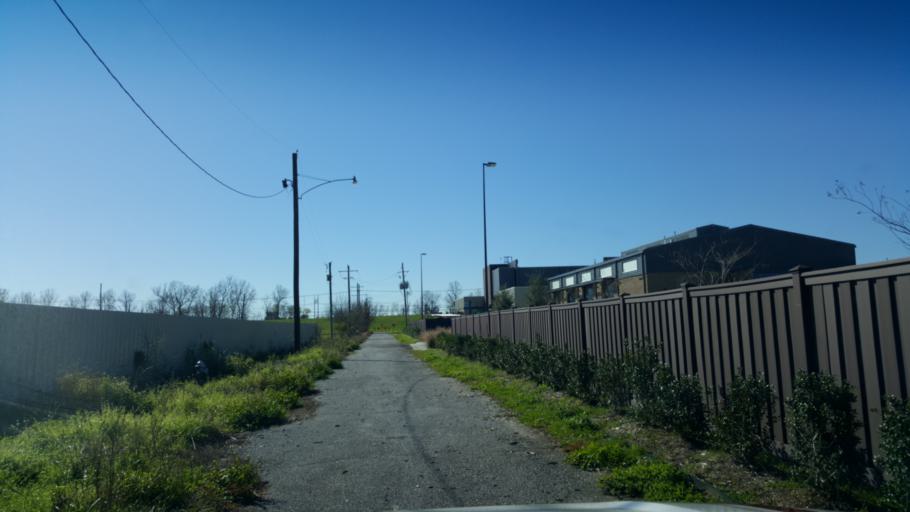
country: US
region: Louisiana
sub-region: Jefferson Parish
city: Kenner
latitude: 29.9770
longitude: -90.2557
